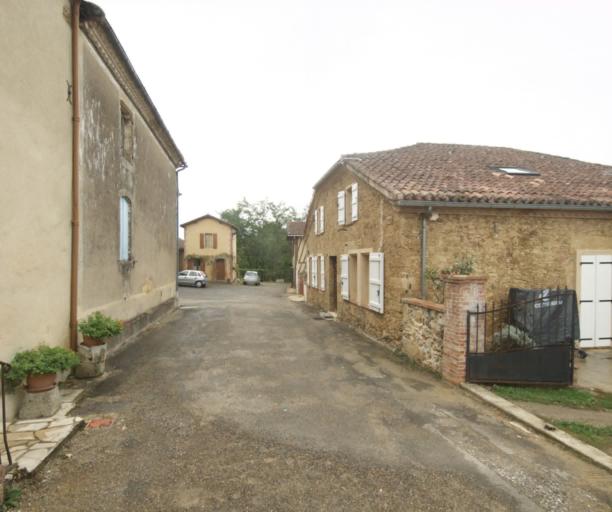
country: FR
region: Midi-Pyrenees
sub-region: Departement du Gers
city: Cazaubon
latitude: 43.9039
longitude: -0.1533
